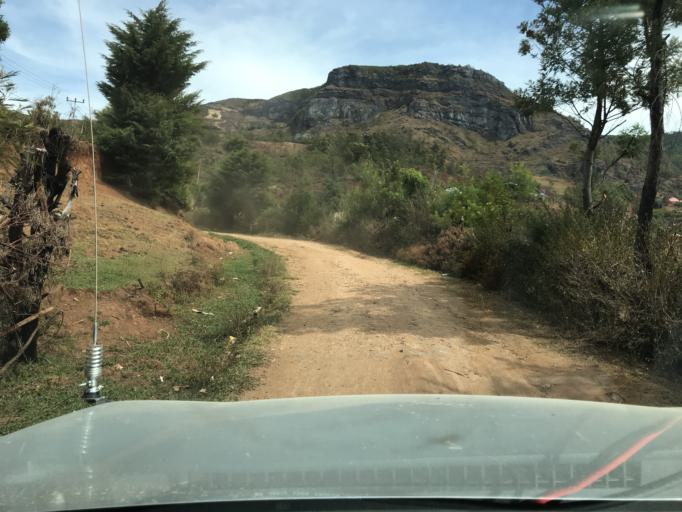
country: TL
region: Ainaro
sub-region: Ainaro
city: Ainaro
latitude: -8.8891
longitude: 125.5197
